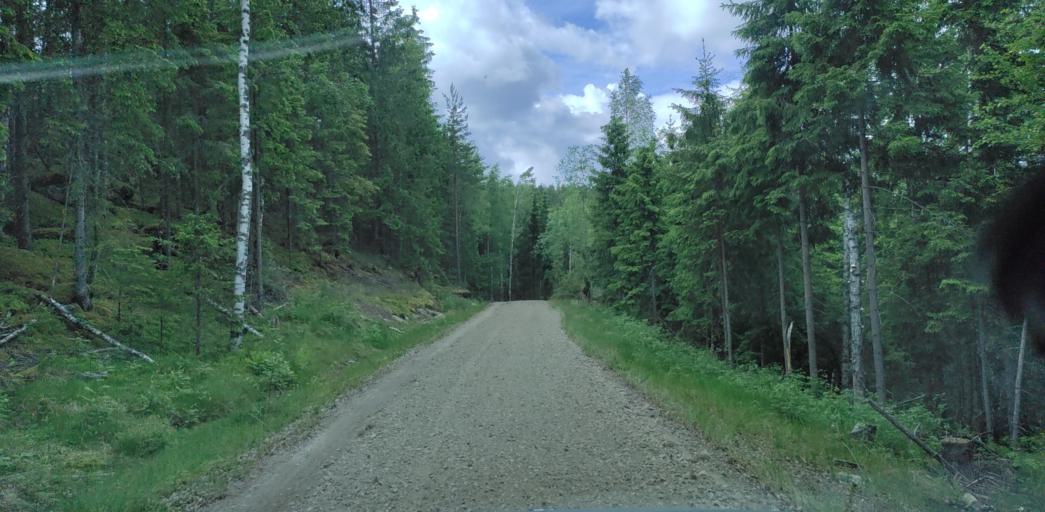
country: SE
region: Vaermland
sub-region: Munkfors Kommun
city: Munkfors
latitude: 59.9694
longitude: 13.4097
